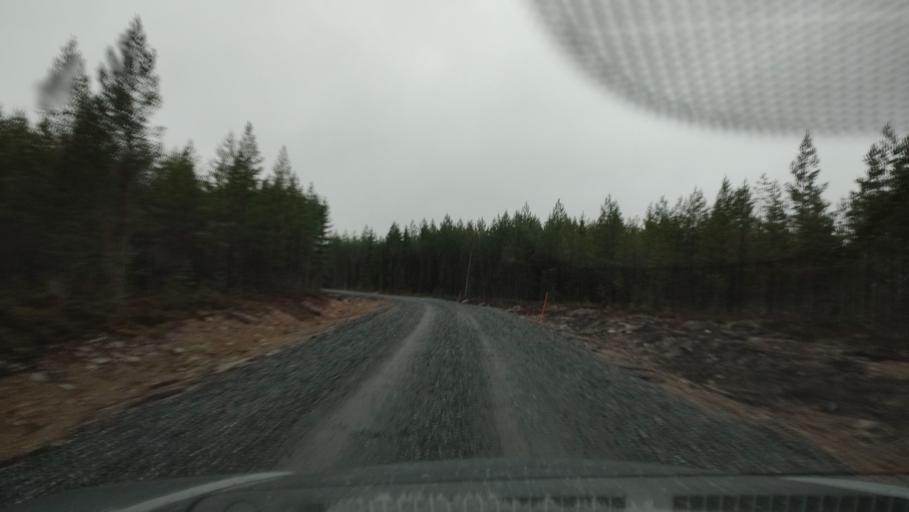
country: FI
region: Southern Ostrobothnia
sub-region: Suupohja
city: Karijoki
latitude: 62.1488
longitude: 21.6163
